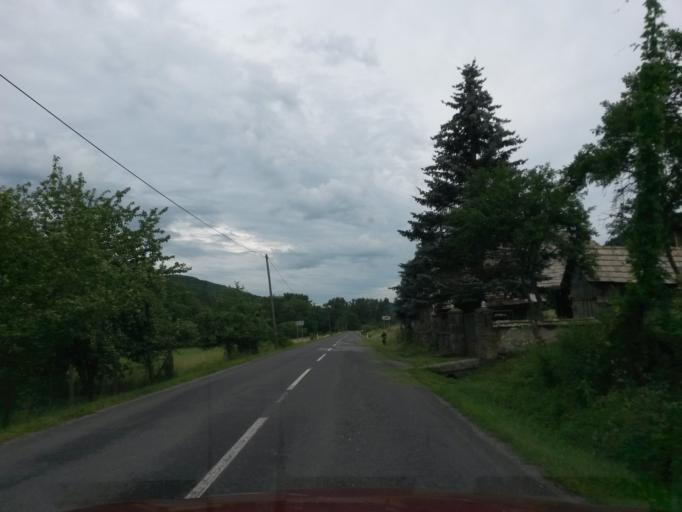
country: SK
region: Banskobystricky
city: Velky Krtis
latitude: 48.3532
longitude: 19.4073
